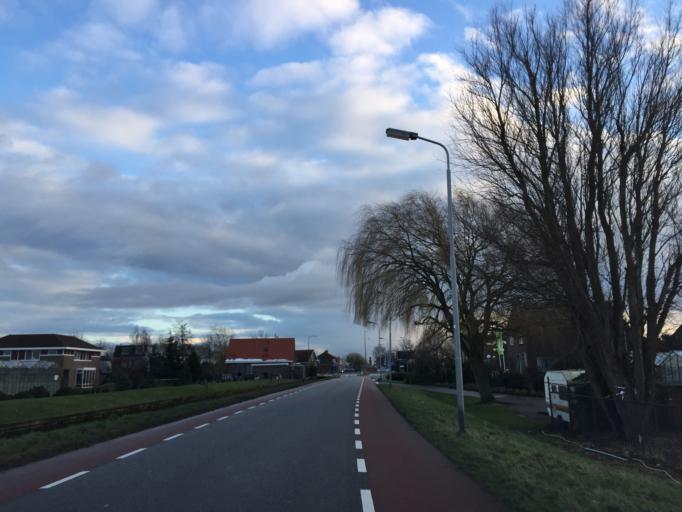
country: NL
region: South Holland
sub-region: Gemeente Pijnacker-Nootdorp
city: Pijnacker
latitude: 52.0182
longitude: 4.4207
